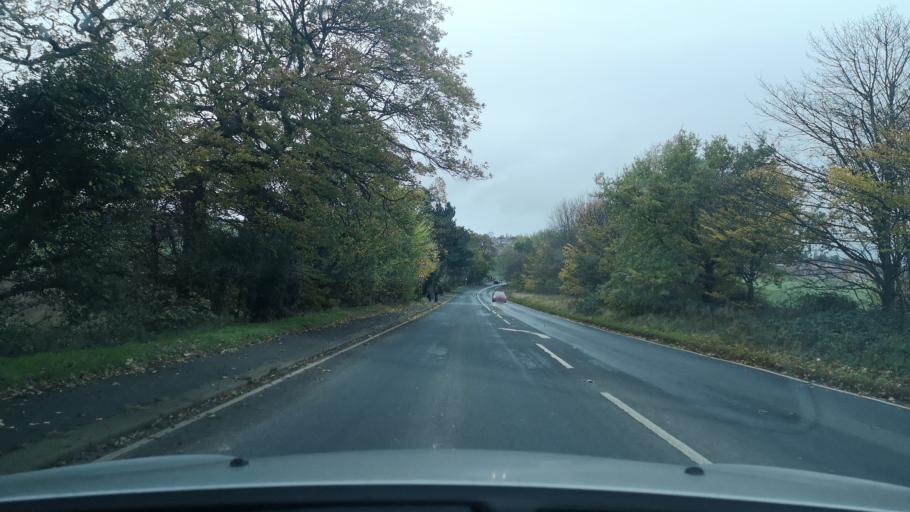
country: GB
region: England
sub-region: City and Borough of Wakefield
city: Low Ackworth
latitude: 53.6696
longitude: -1.3239
